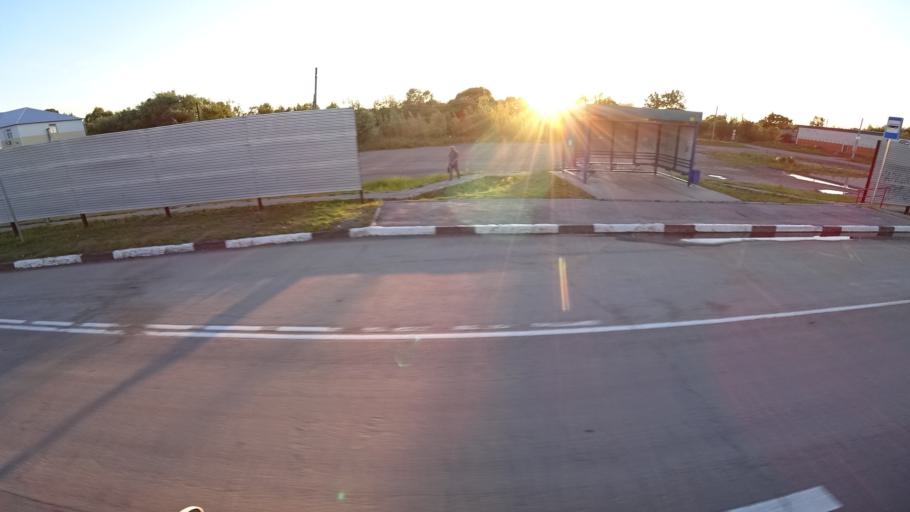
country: RU
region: Khabarovsk Krai
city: Khor
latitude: 47.8525
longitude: 134.9608
